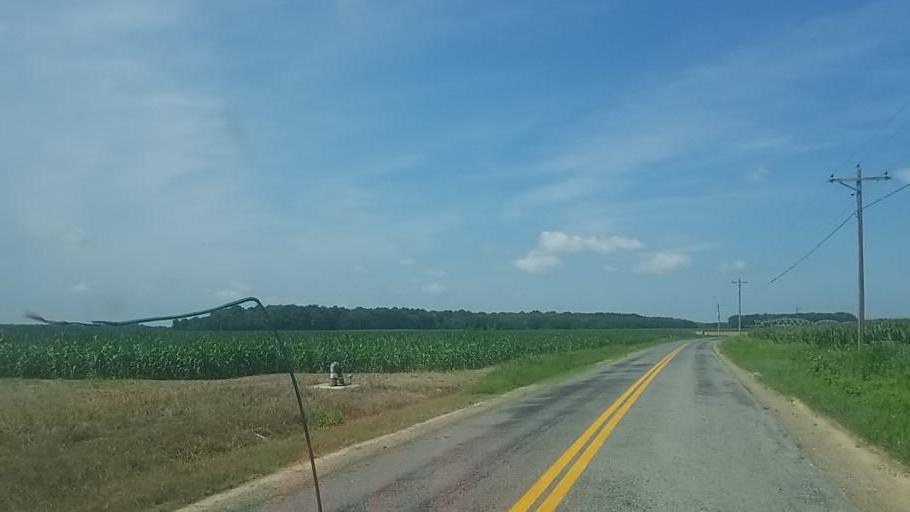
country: US
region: Maryland
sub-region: Caroline County
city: Denton
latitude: 38.8719
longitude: -75.7512
